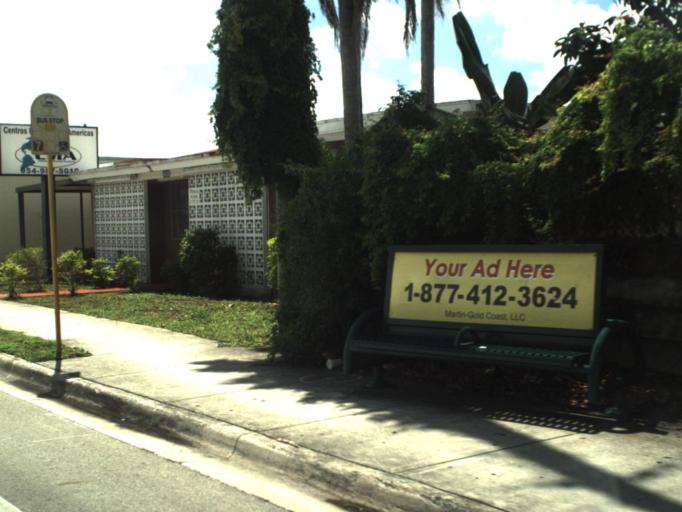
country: US
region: Florida
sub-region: Broward County
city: Pembroke Pines
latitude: 26.0096
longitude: -80.2238
